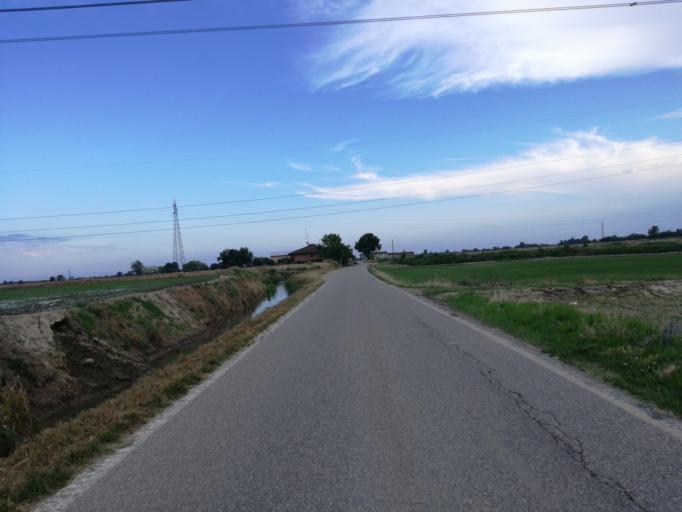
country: IT
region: Piedmont
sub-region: Provincia di Novara
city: Torrion Quartara
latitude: 45.4146
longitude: 8.6191
